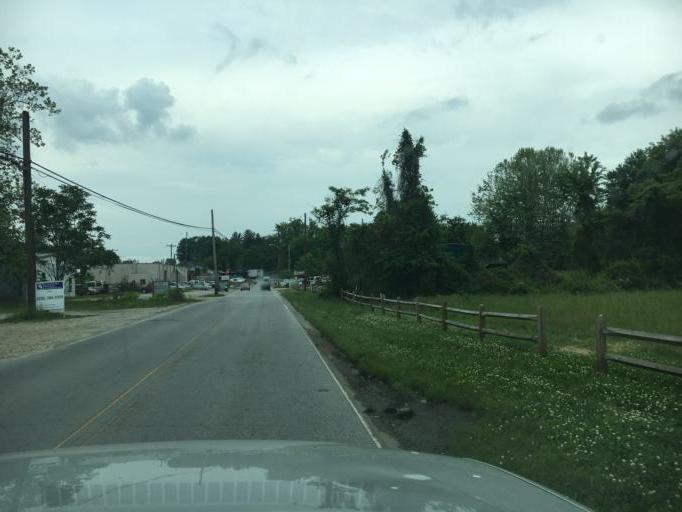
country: US
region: North Carolina
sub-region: Henderson County
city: Hendersonville
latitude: 35.3118
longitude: -82.4563
